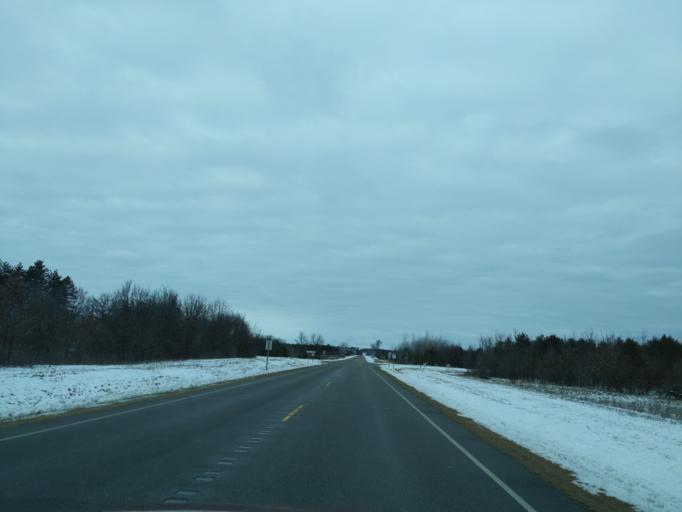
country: US
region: Wisconsin
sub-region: Waushara County
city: Wautoma
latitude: 43.9811
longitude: -89.3276
